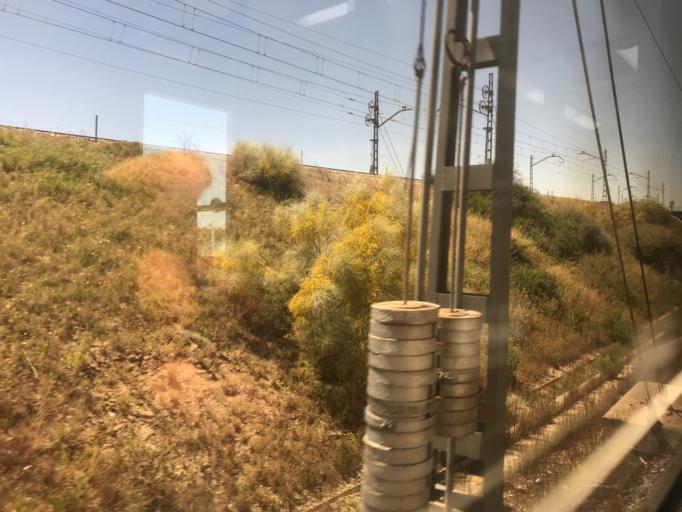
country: ES
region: Madrid
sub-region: Provincia de Madrid
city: Puente de Vallecas
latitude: 40.3839
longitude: -3.6800
